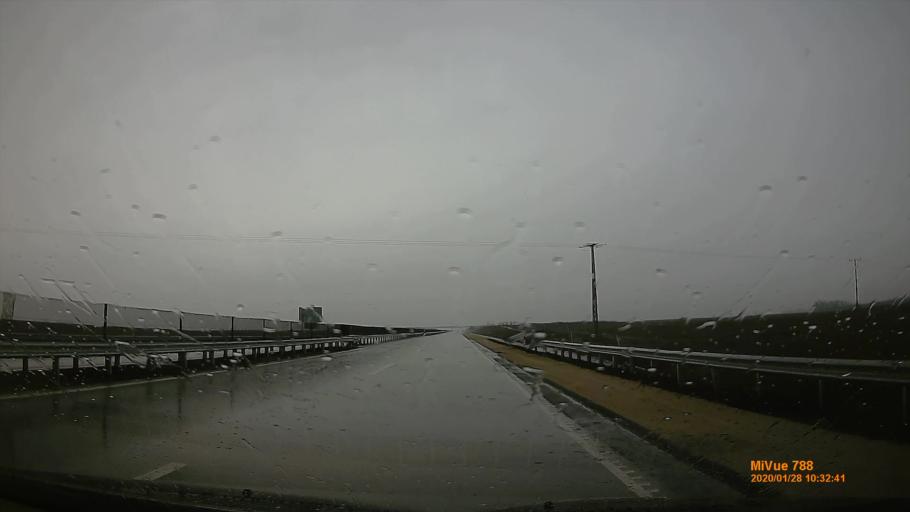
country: HU
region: Pest
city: Monor
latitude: 47.3519
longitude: 19.4909
